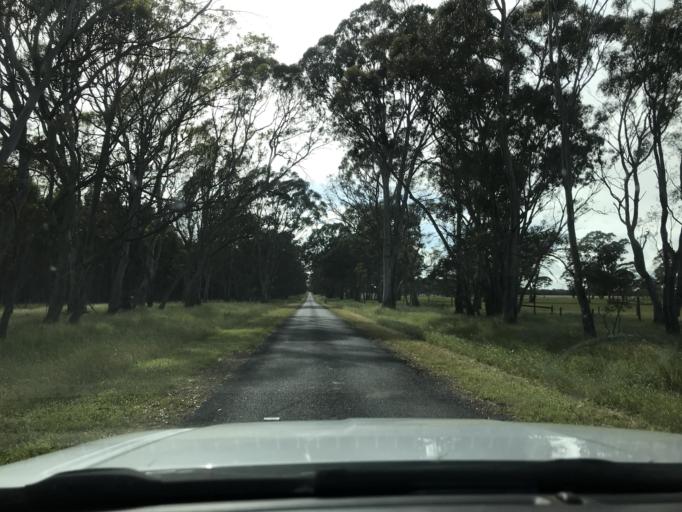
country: AU
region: South Australia
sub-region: Wattle Range
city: Penola
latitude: -37.1872
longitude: 141.2254
